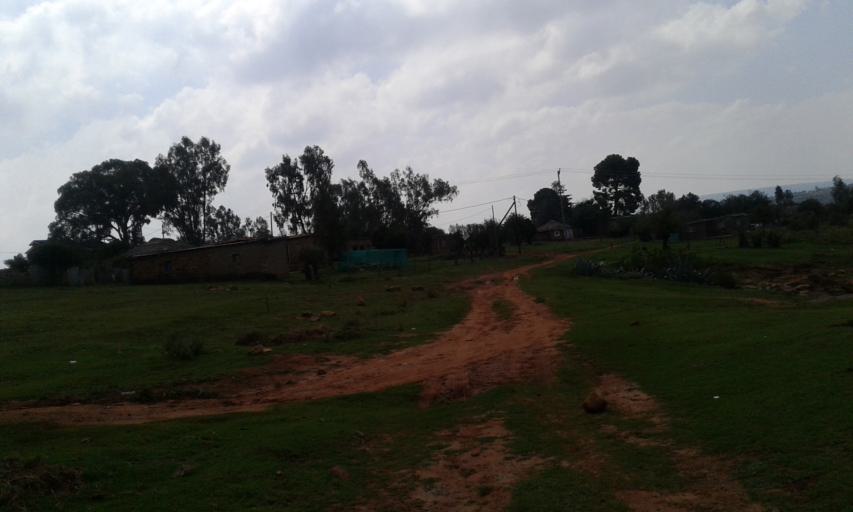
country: LS
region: Maseru
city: Maseru
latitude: -29.4259
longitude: 27.5742
